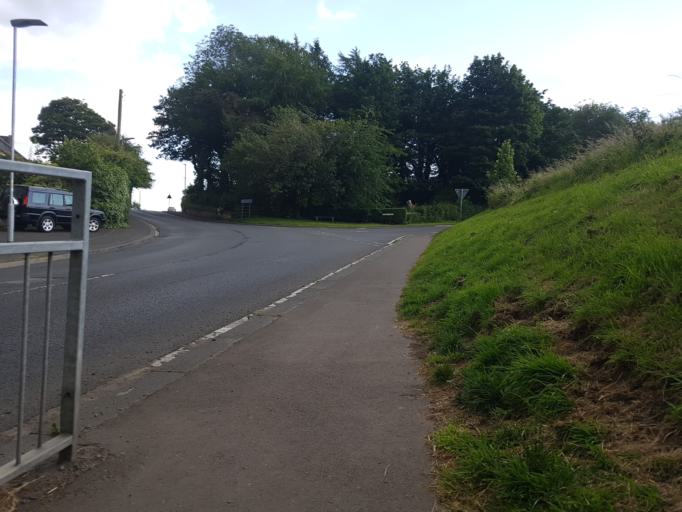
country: GB
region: England
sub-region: Northumberland
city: Alnmouth
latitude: 55.3951
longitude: -1.6333
